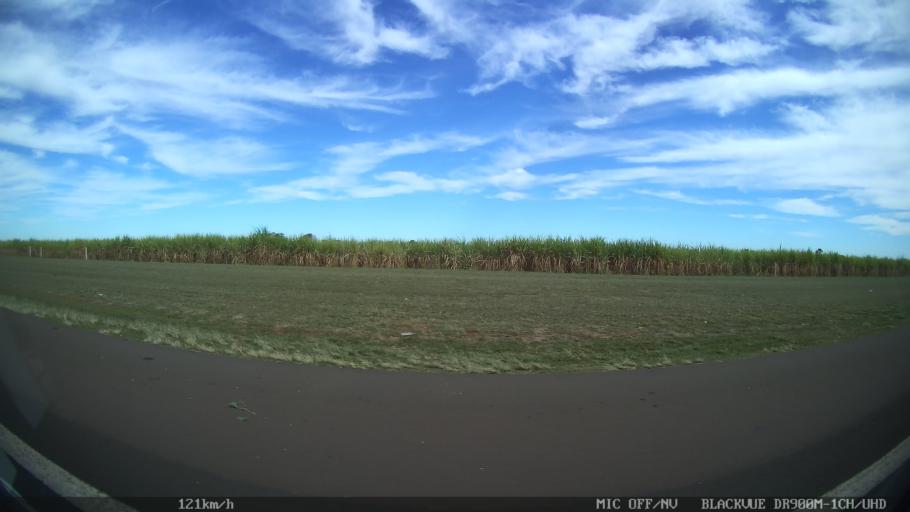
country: BR
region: Sao Paulo
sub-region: Taquaritinga
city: Taquaritinga
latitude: -21.4861
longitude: -48.5837
